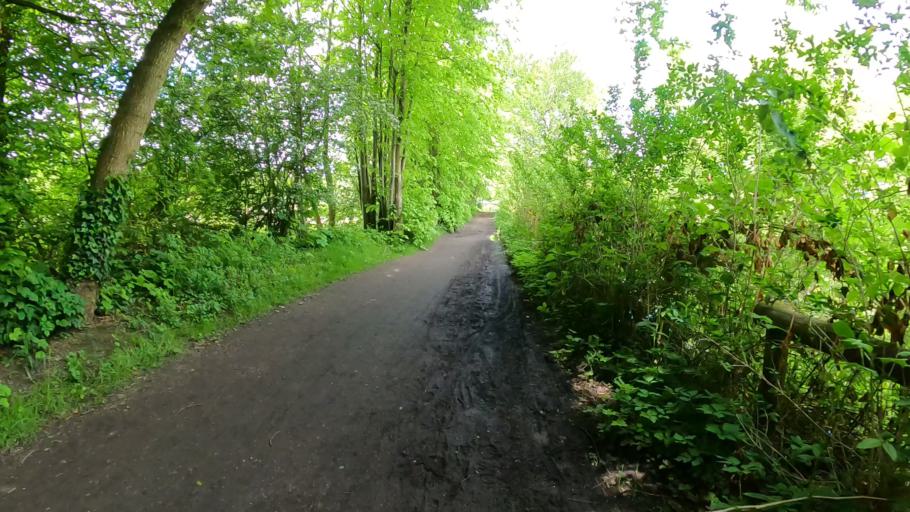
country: DE
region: Hamburg
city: Wohldorf-Ohlstedt
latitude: 53.7091
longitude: 10.1337
